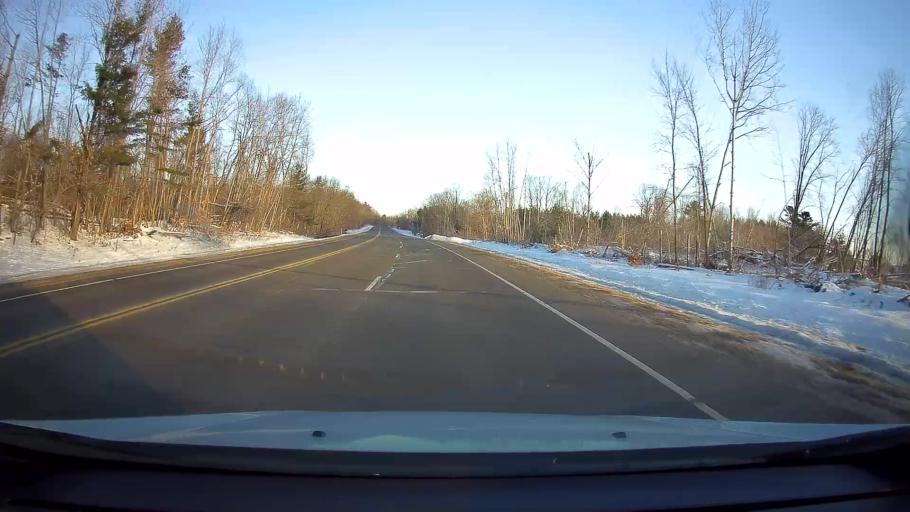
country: US
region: Wisconsin
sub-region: Barron County
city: Turtle Lake
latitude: 45.4298
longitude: -92.1293
